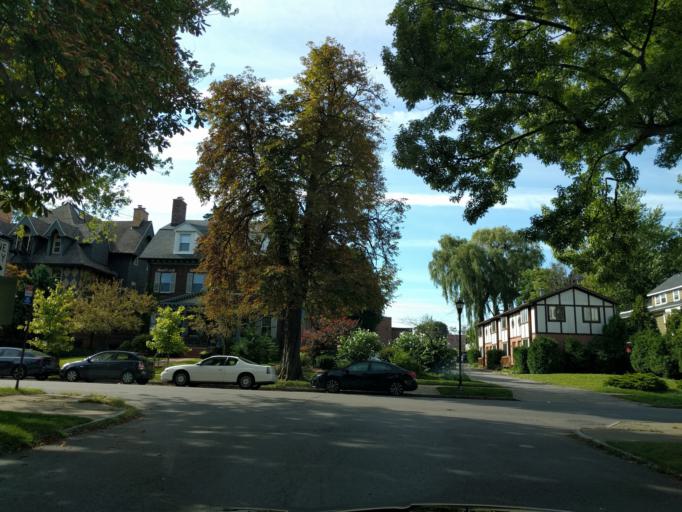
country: US
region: New York
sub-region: Erie County
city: Buffalo
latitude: 42.9050
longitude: -78.8803
